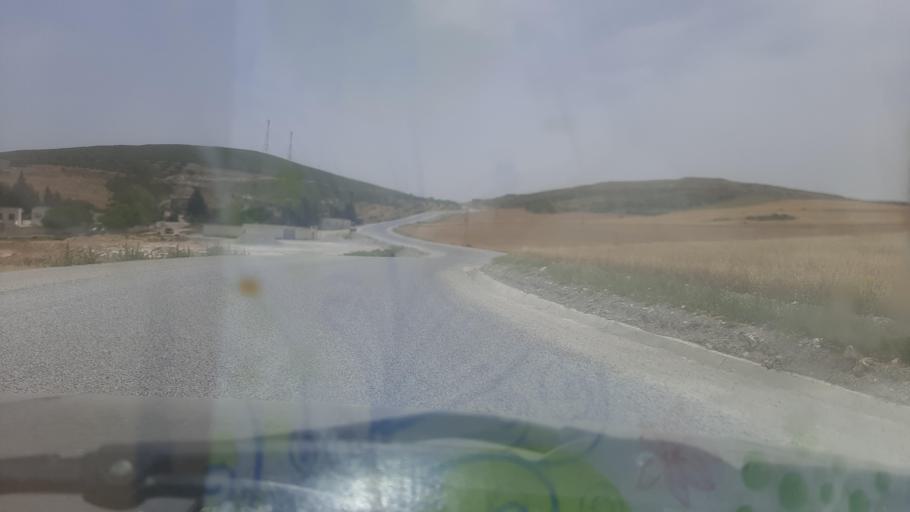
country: TN
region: Zaghwan
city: Zaghouan
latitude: 36.5382
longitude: 10.1531
